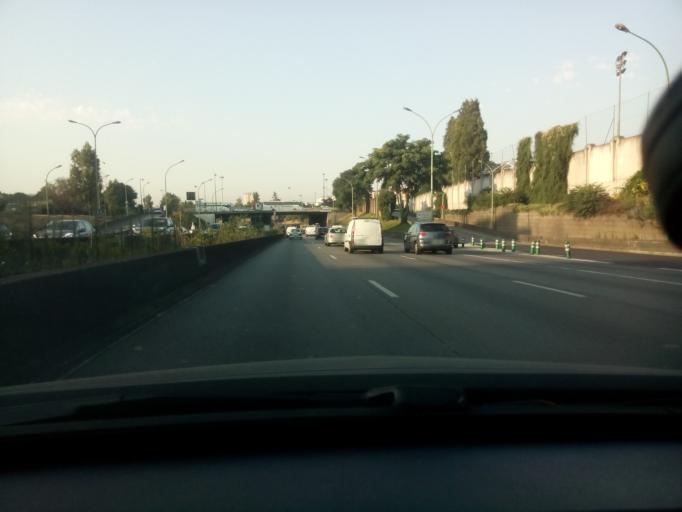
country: FR
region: Ile-de-France
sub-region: Departement de Seine-Saint-Denis
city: Bagnolet
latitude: 48.8565
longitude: 2.4140
